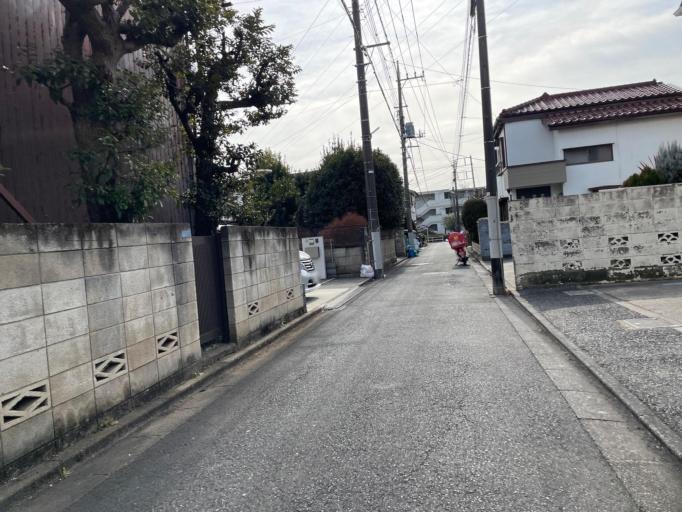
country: JP
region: Tokyo
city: Kamirenjaku
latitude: 35.6984
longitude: 139.5350
